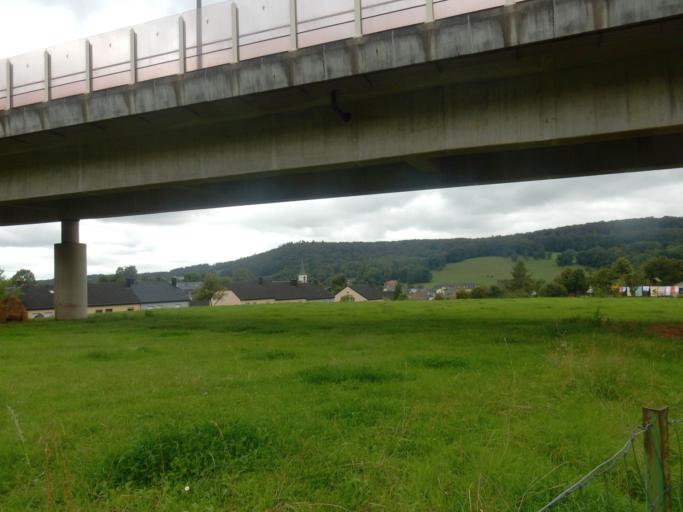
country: LU
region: Diekirch
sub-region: Canton de Diekirch
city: Schieren
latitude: 49.8328
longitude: 6.0996
